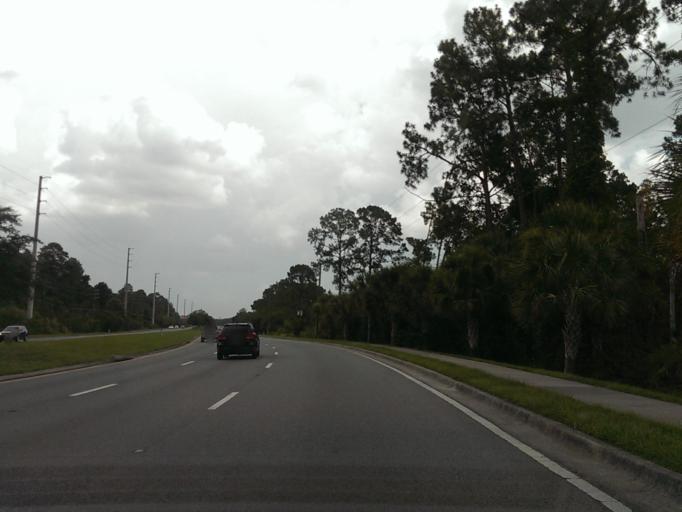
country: US
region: Florida
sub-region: Osceola County
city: Celebration
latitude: 28.3861
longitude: -81.5151
